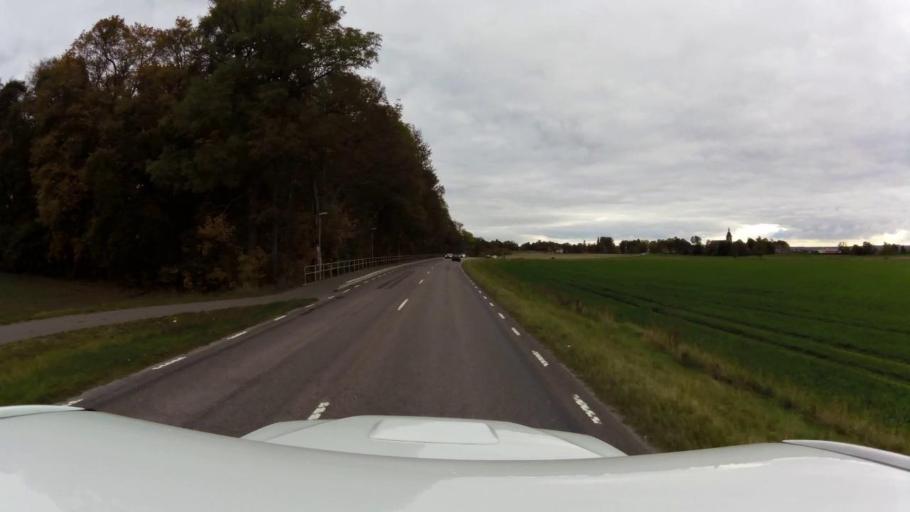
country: SE
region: OEstergoetland
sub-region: Linkopings Kommun
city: Berg
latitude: 58.4876
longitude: 15.5106
